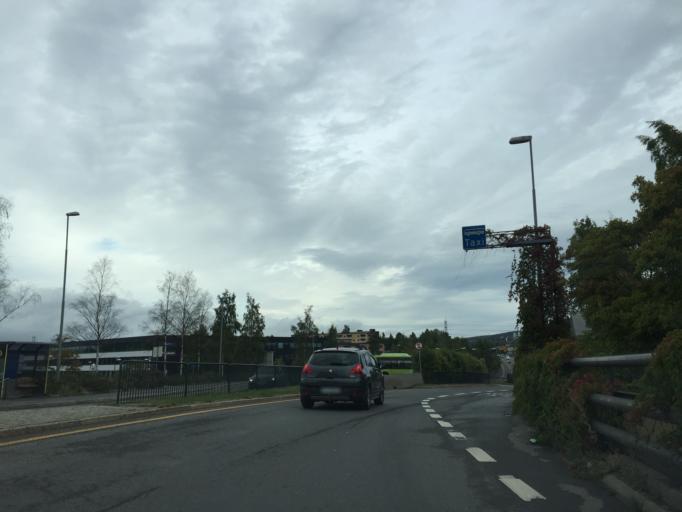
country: NO
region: Oslo
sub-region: Oslo
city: Oslo
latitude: 59.8950
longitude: 10.8049
